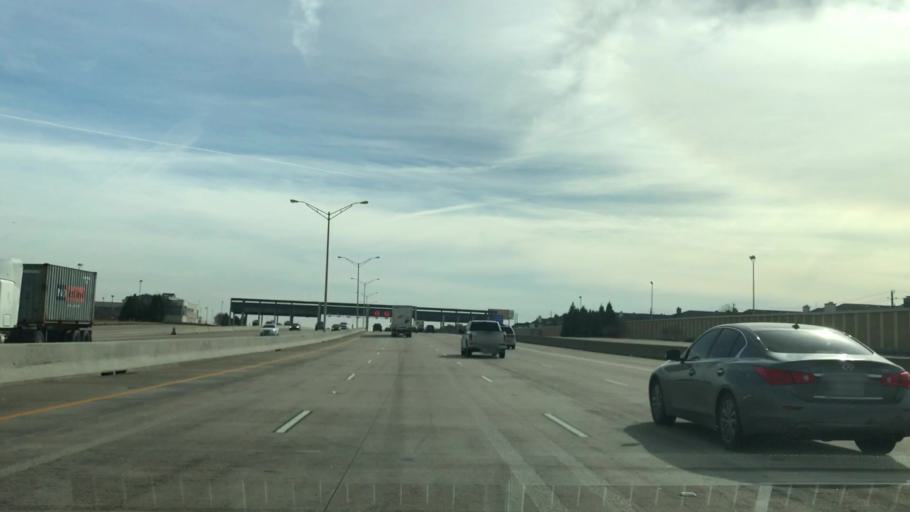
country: US
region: Texas
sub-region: Dallas County
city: Addison
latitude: 33.0040
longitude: -96.7794
